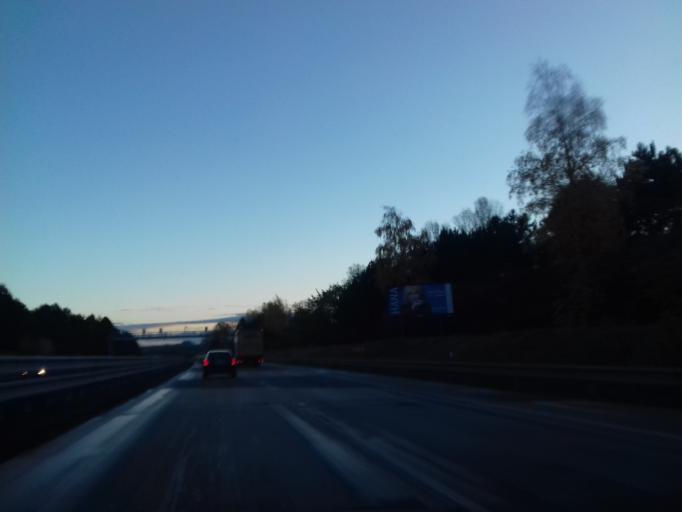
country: CZ
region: South Moravian
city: Rousinov
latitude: 49.2011
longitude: 16.9015
